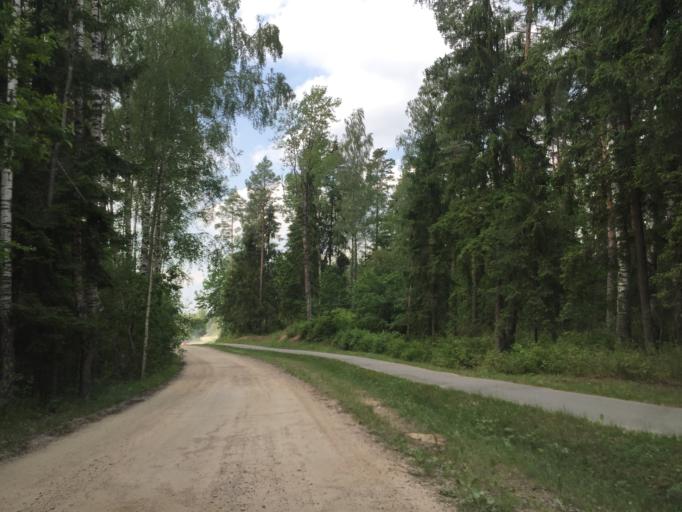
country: LV
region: Olaine
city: Olaine
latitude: 56.7753
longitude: 23.9069
